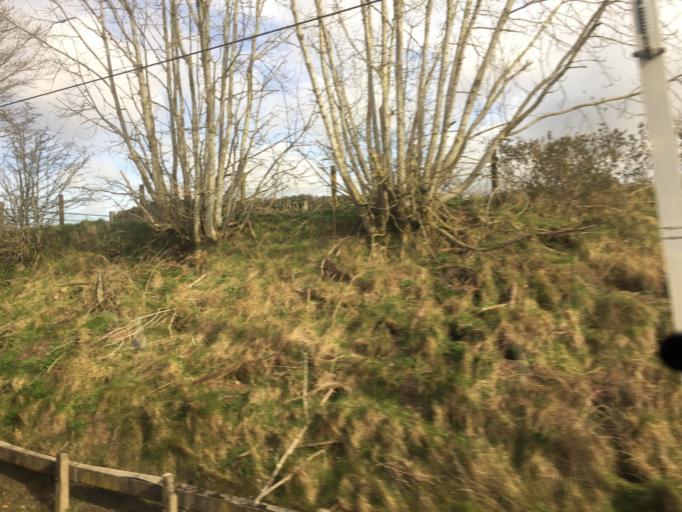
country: GB
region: England
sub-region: Cumbria
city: Penrith
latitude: 54.6406
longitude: -2.7563
